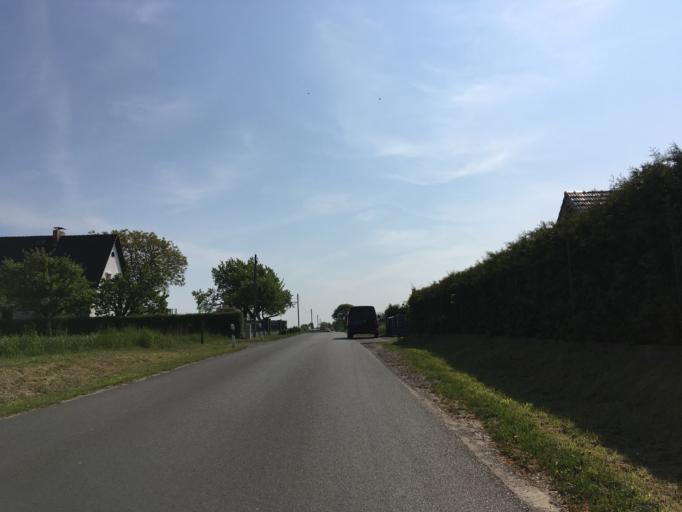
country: DE
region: Berlin
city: Hellersdorf
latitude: 52.5690
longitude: 13.6245
